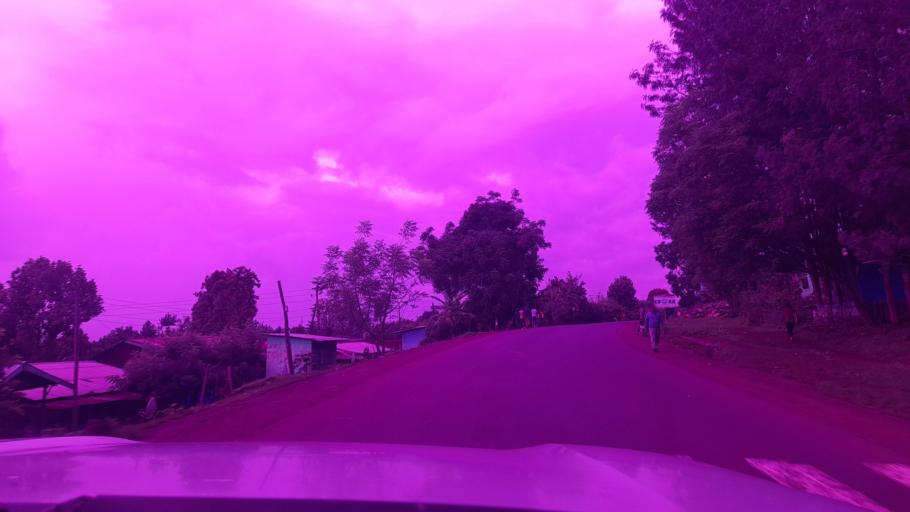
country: ET
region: Oromiya
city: Jima
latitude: 7.9641
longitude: 37.4402
